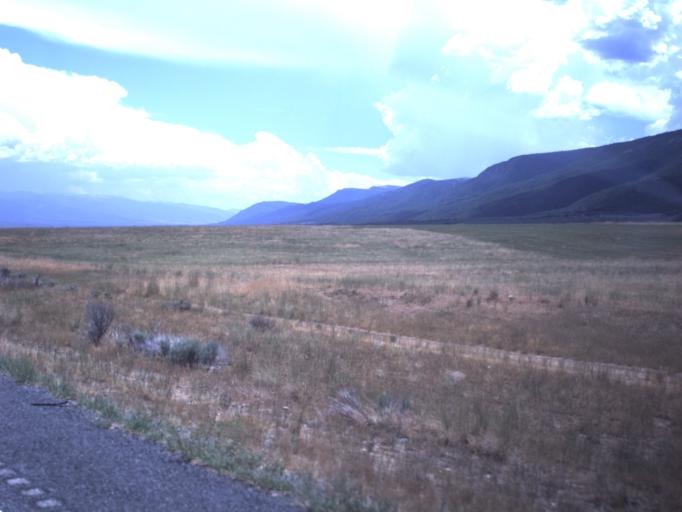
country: US
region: Utah
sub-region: Sanpete County
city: Fountain Green
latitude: 39.6598
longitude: -111.6545
